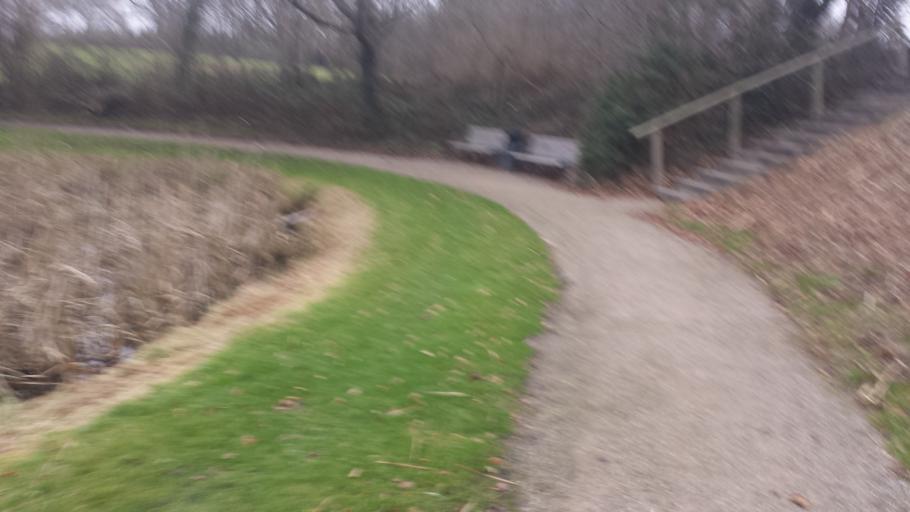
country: DK
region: South Denmark
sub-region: Sonderborg Kommune
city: Grasten
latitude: 54.9063
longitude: 9.5889
